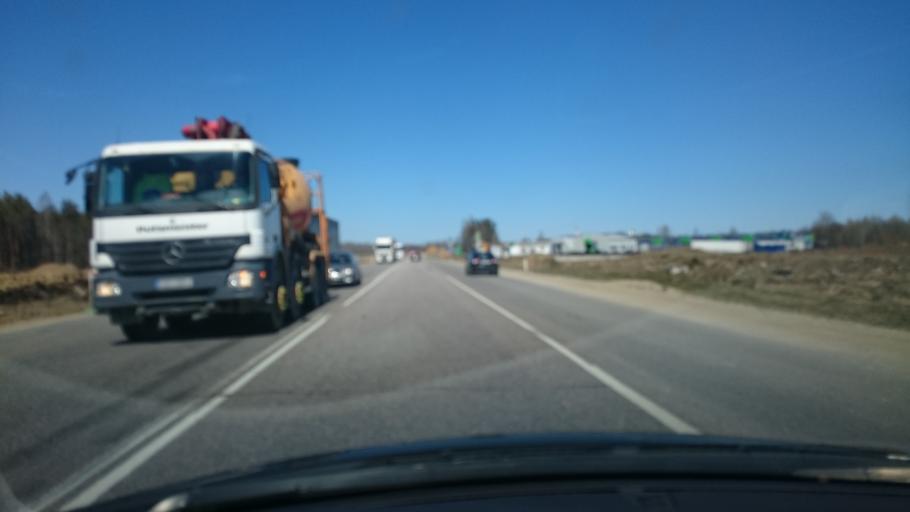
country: EE
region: Harju
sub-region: Joelaehtme vald
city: Loo
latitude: 59.3984
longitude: 24.9171
